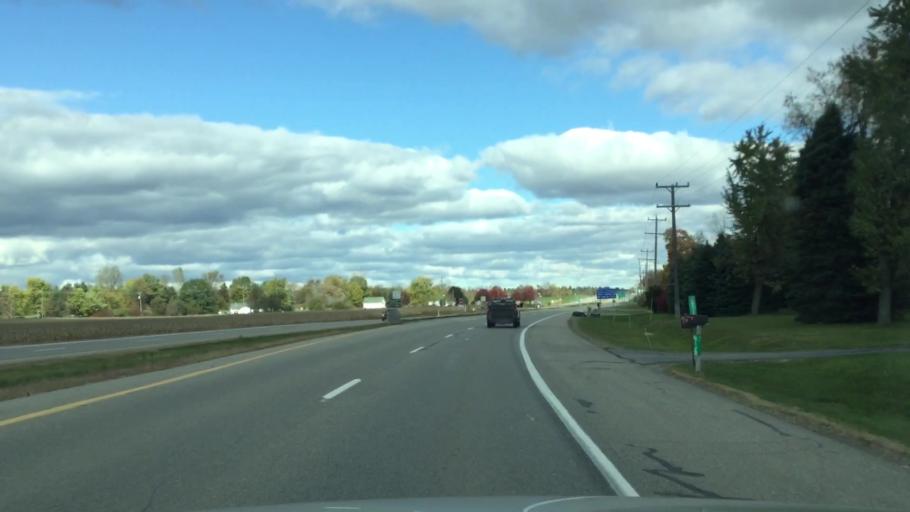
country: US
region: Michigan
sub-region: Lapeer County
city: Lapeer
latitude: 42.9964
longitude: -83.3208
